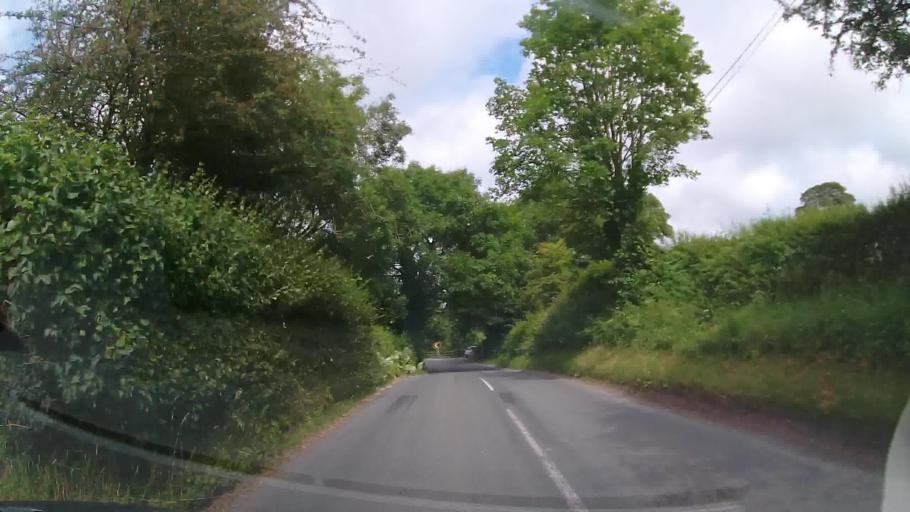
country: GB
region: Wales
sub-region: Sir Powys
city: Llanrhaeadr-ym-Mochnant
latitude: 52.8102
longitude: -3.3149
